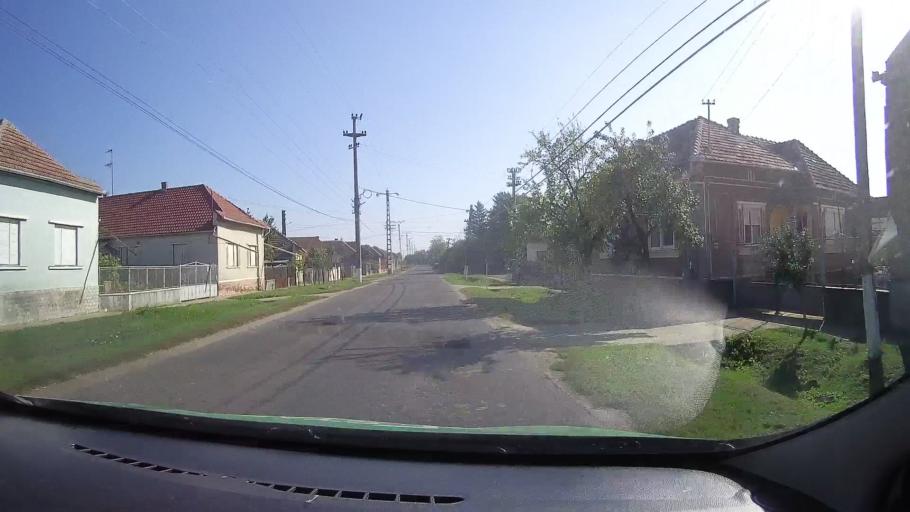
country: RO
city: Foieni
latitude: 47.6959
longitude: 22.3931
